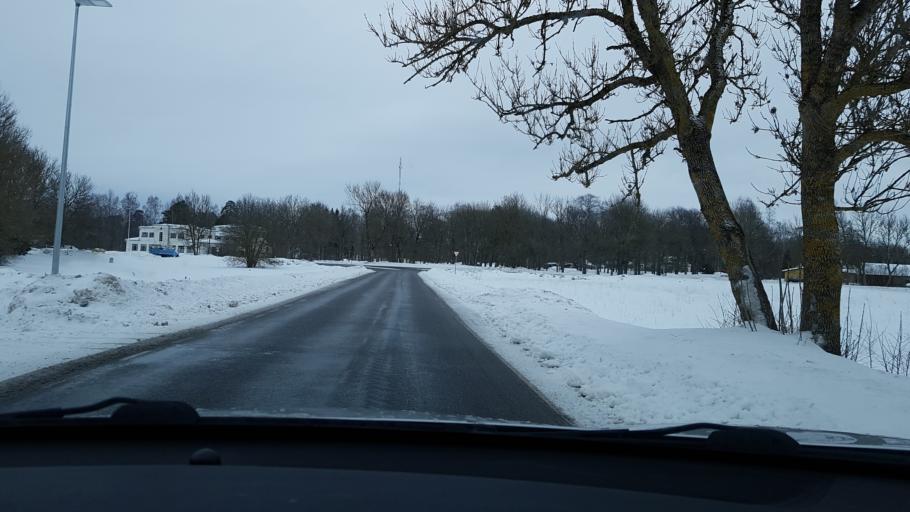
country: EE
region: Jaervamaa
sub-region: Jaerva-Jaani vald
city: Jarva-Jaani
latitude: 59.1390
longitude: 25.7527
